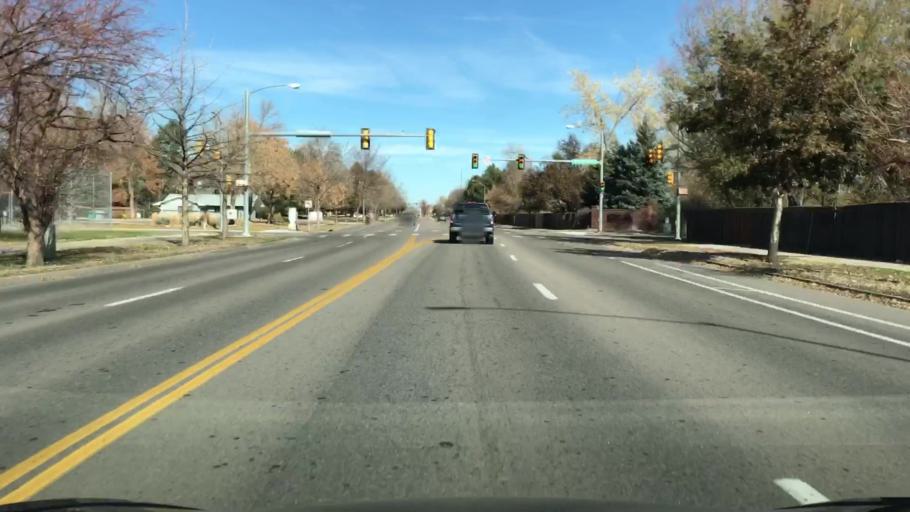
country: US
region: Colorado
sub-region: Larimer County
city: Fort Collins
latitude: 40.5487
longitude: -105.0961
